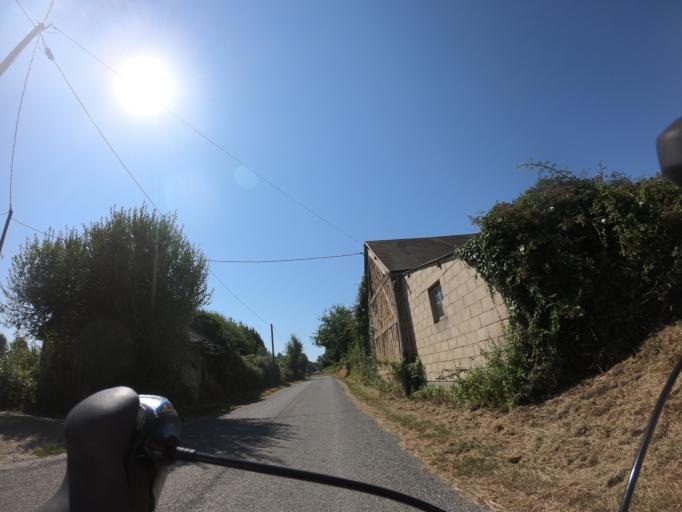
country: FR
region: Lower Normandy
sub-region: Departement de la Manche
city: Barenton
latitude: 48.5724
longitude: -0.8001
